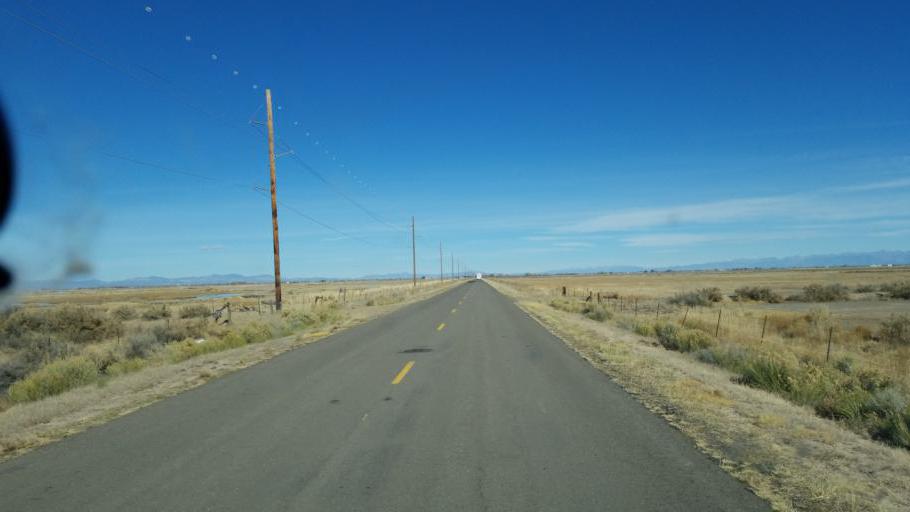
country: US
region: Colorado
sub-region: Rio Grande County
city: Monte Vista
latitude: 37.4873
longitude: -106.0941
